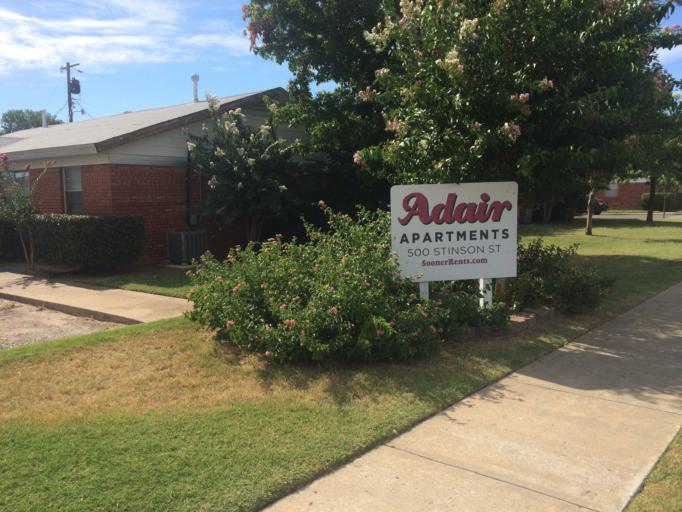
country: US
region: Oklahoma
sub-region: Cleveland County
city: Norman
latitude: 35.2004
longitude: -97.4368
